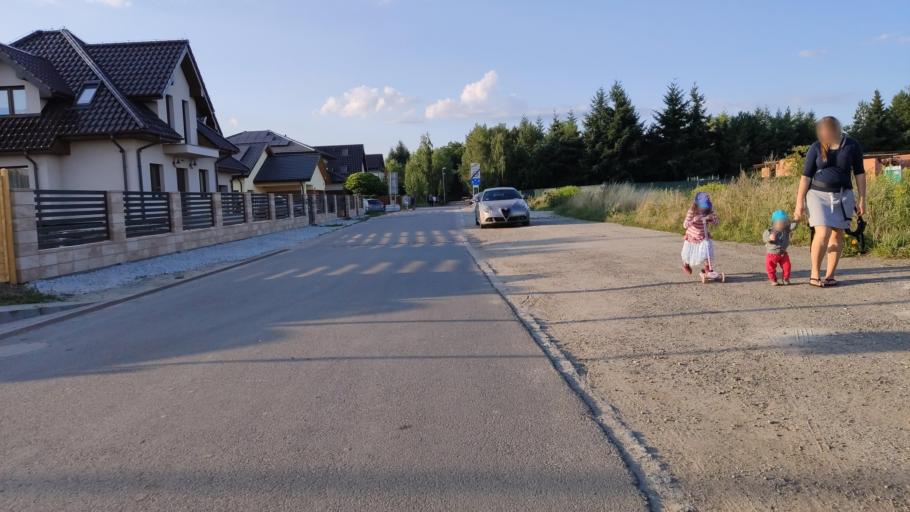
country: PL
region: Lower Silesian Voivodeship
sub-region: Powiat wroclawski
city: Zerniki Wroclawskie
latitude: 51.0536
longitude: 17.0661
